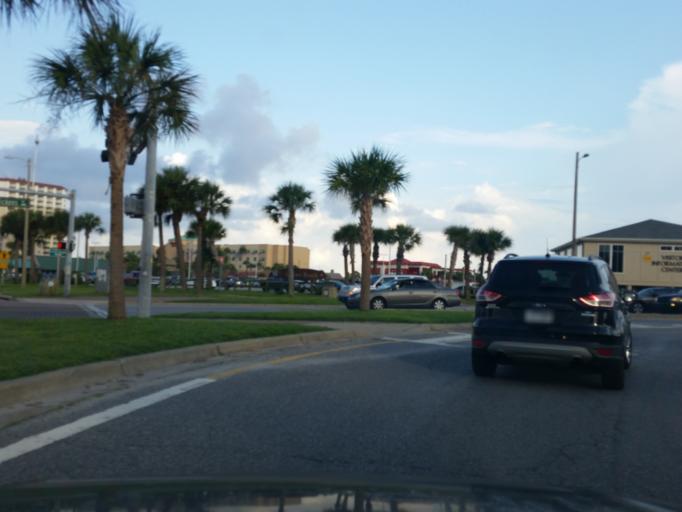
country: US
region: Florida
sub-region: Santa Rosa County
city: Gulf Breeze
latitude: 30.3337
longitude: -87.1415
